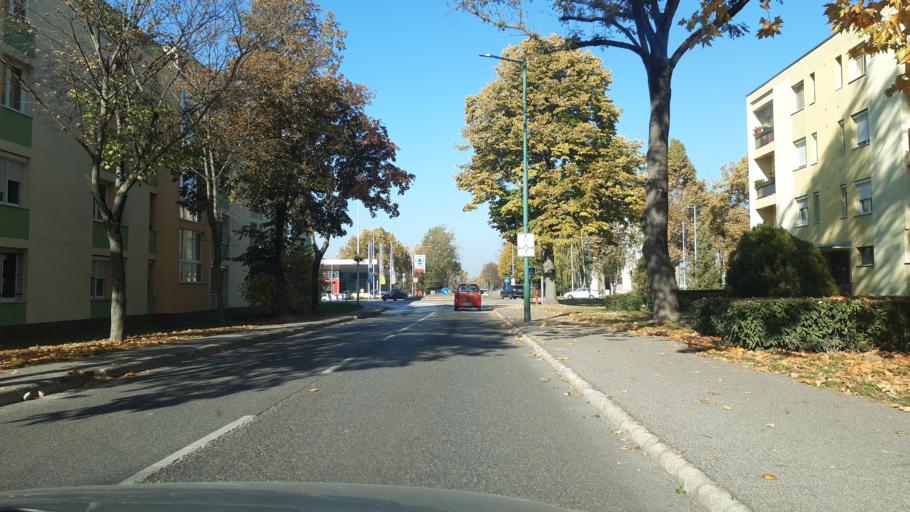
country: HU
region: Veszprem
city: Ajka
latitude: 47.1079
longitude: 17.5527
